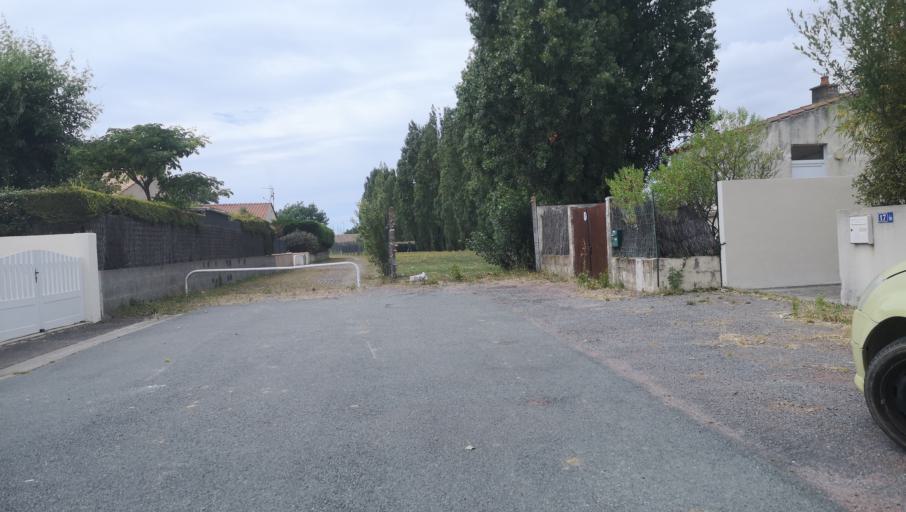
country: FR
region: Pays de la Loire
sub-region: Departement de la Vendee
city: Les Sables-d'Olonne
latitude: 46.5089
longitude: -1.7733
